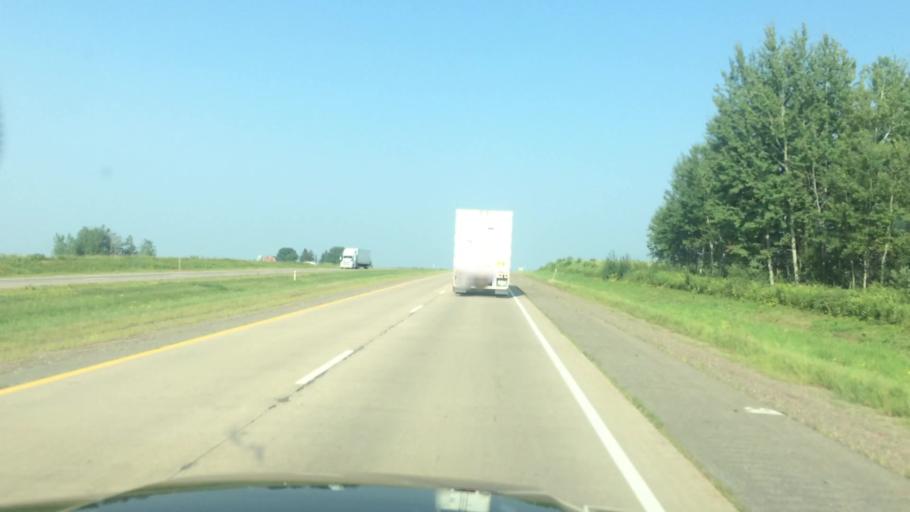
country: US
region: Wisconsin
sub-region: Marathon County
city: Athens
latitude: 44.9442
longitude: -90.0552
